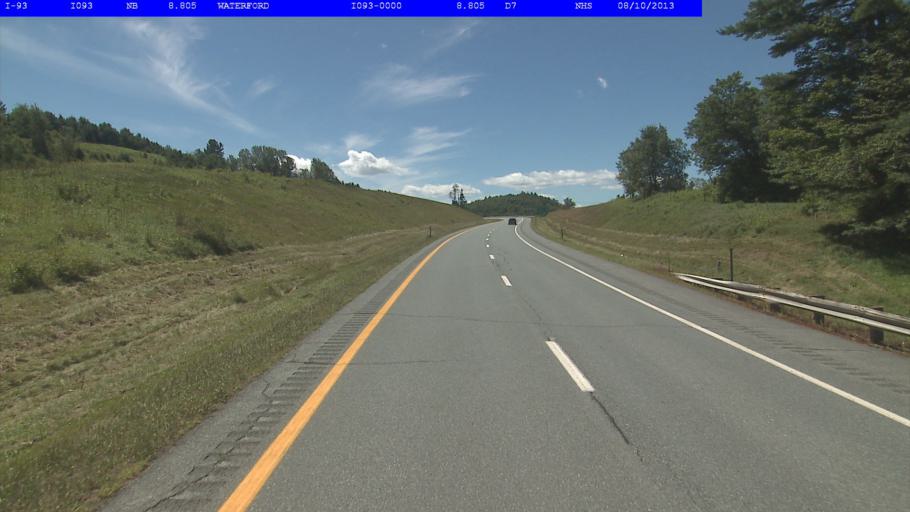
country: US
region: Vermont
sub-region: Caledonia County
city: Saint Johnsbury
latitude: 44.4172
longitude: -71.9778
